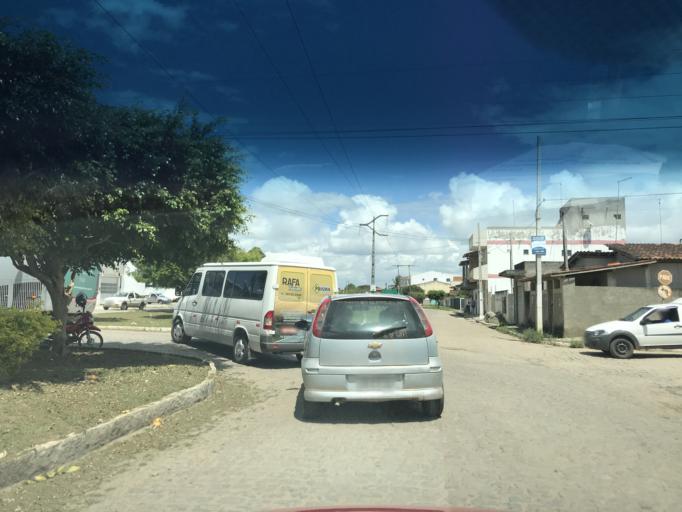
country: BR
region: Bahia
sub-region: Cruz Das Almas
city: Cruz das Almas
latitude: -12.6661
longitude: -39.1130
